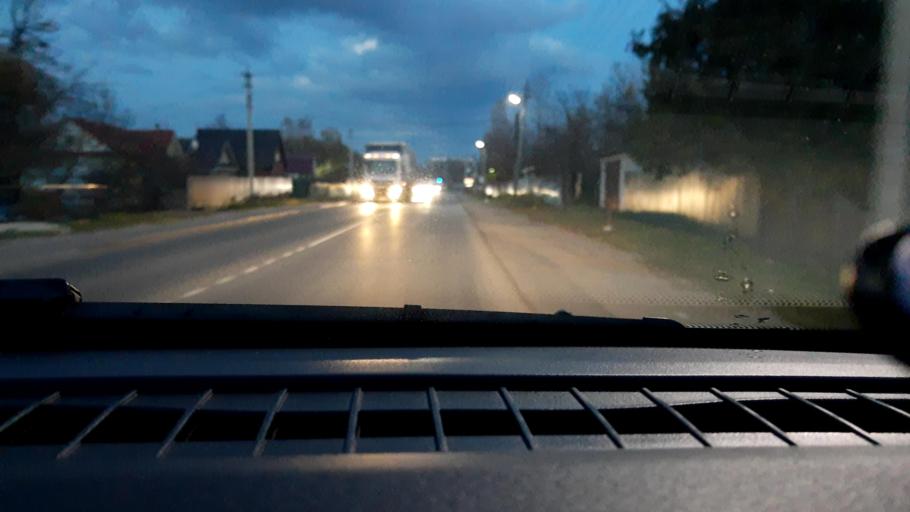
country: RU
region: Nizjnij Novgorod
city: Novaya Balakhna
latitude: 56.4845
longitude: 43.5738
